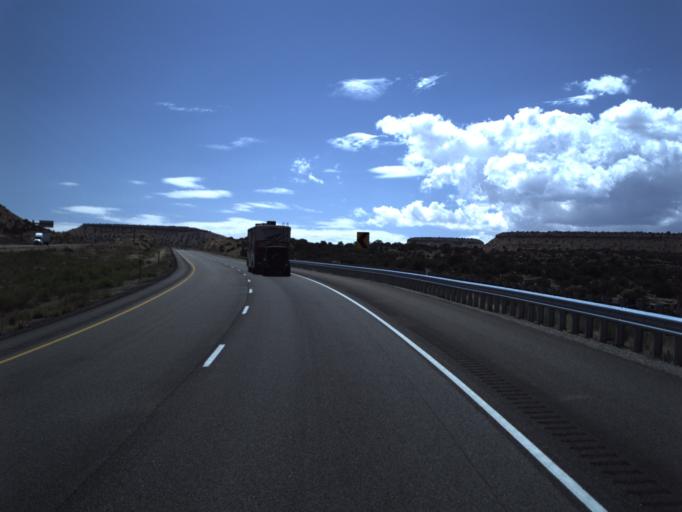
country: US
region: Utah
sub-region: Emery County
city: Castle Dale
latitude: 38.9284
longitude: -110.4953
